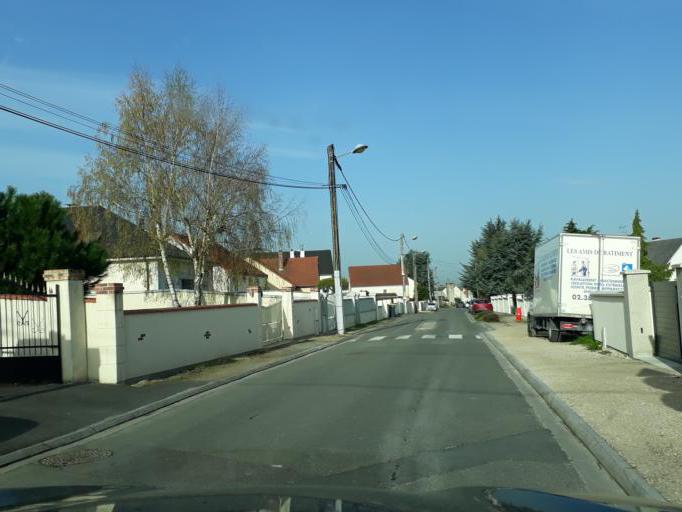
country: FR
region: Centre
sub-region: Departement du Loiret
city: Ingre
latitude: 47.9124
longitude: 1.8300
